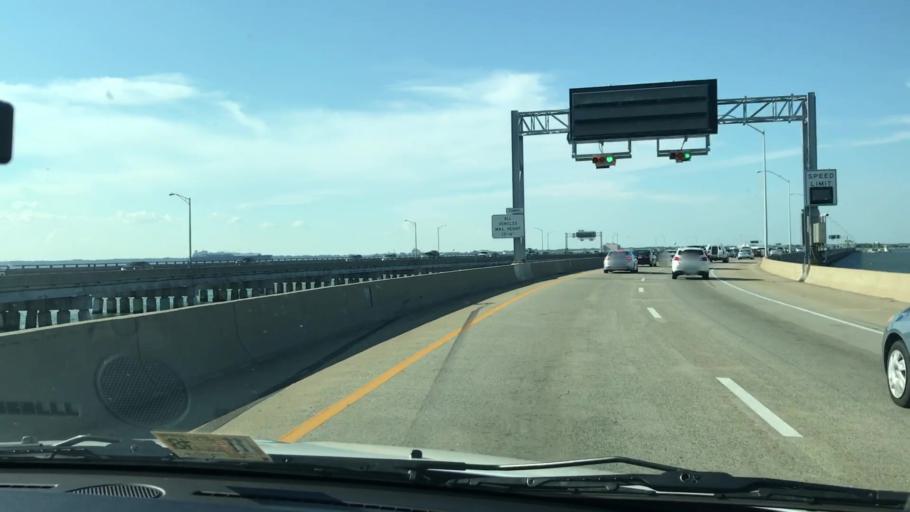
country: US
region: Virginia
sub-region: City of Hampton
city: East Hampton
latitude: 36.9694
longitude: -76.2994
